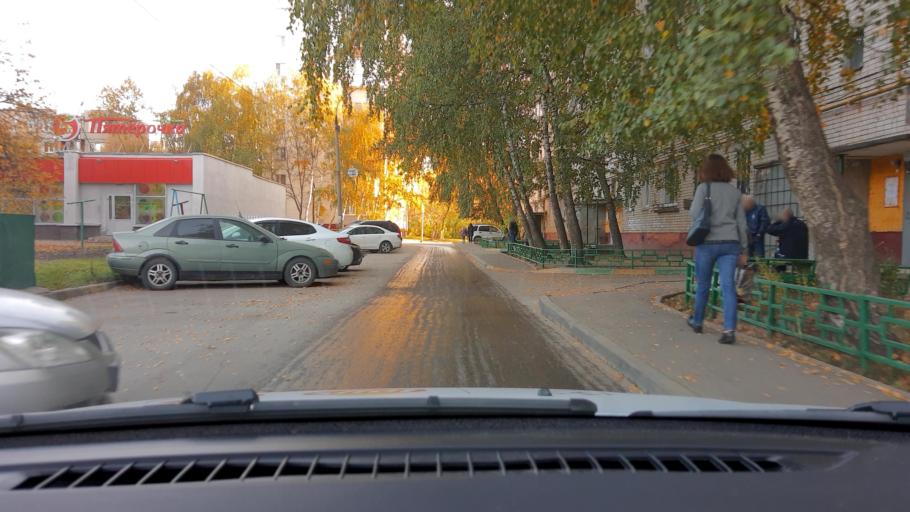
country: RU
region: Nizjnij Novgorod
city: Gorbatovka
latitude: 56.2558
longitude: 43.8815
